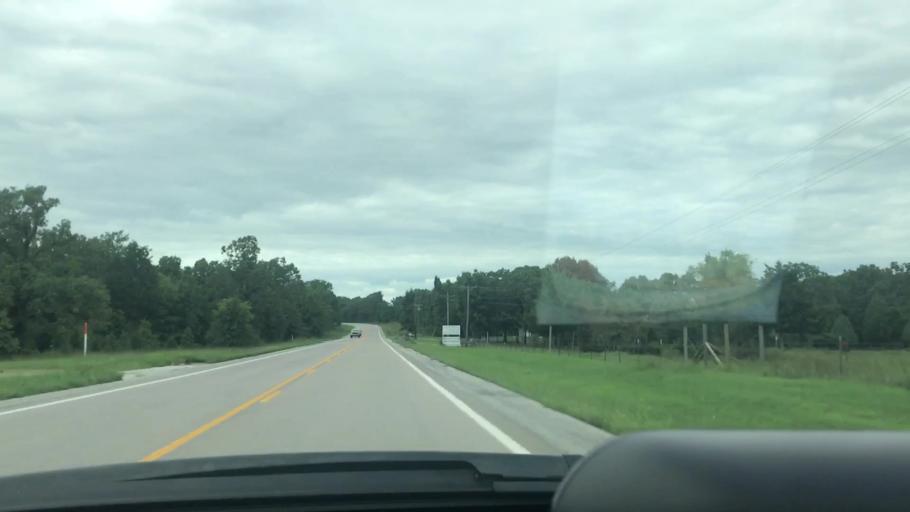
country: US
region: Missouri
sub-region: Benton County
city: Warsaw
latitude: 38.1554
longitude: -93.2966
